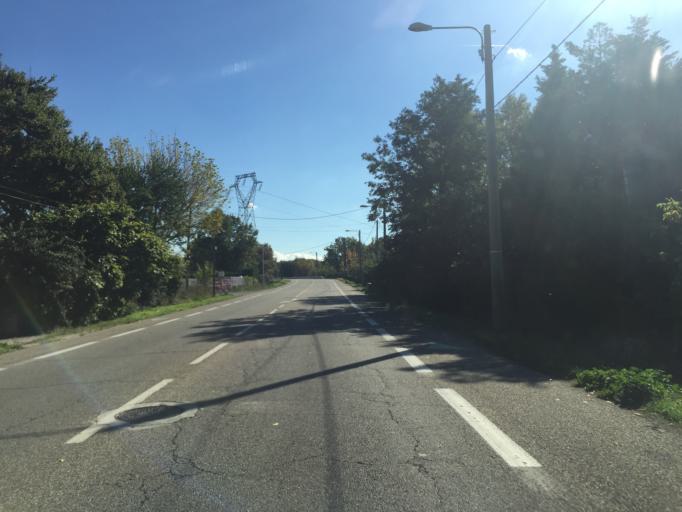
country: FR
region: Provence-Alpes-Cote d'Azur
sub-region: Departement du Vaucluse
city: Montfavet
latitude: 43.9335
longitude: 4.8569
